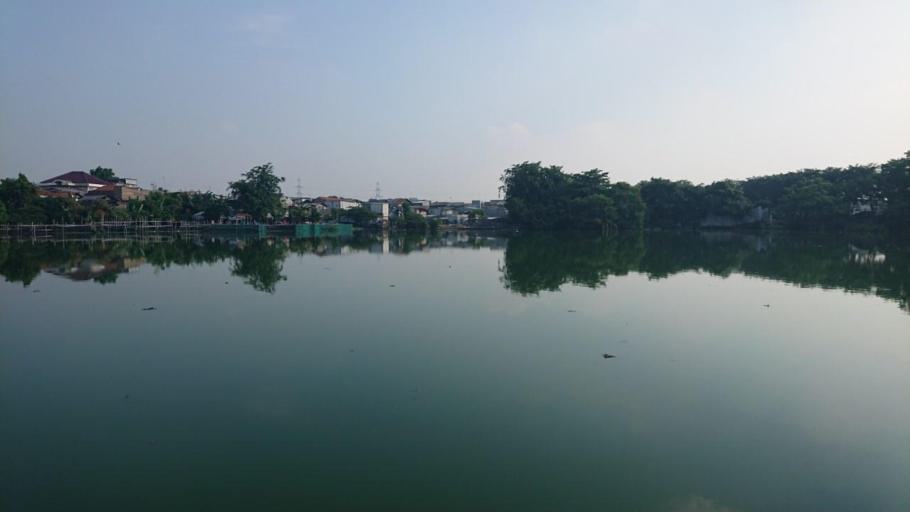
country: ID
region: West Java
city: Bekasi
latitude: -6.2122
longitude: 106.9222
